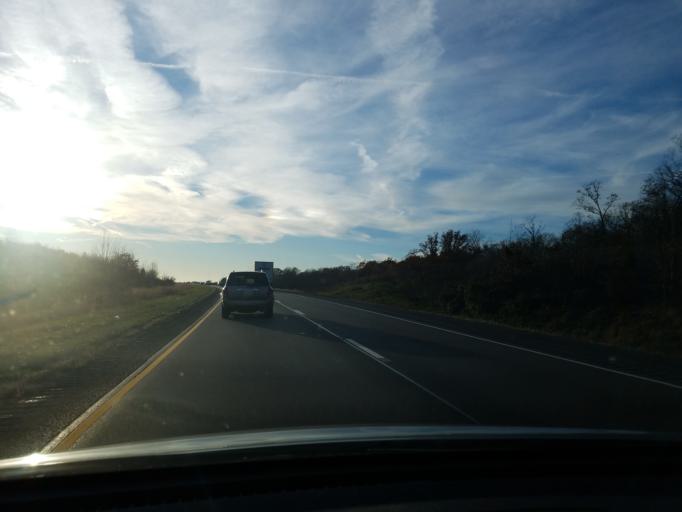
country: US
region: Indiana
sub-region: Dubois County
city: Ferdinand
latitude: 38.2069
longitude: -86.8898
